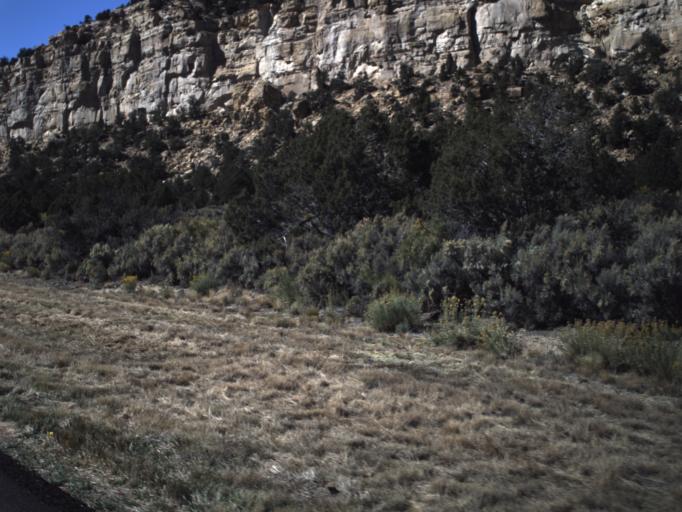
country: US
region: Utah
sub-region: Garfield County
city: Panguitch
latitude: 37.7279
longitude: -111.7687
